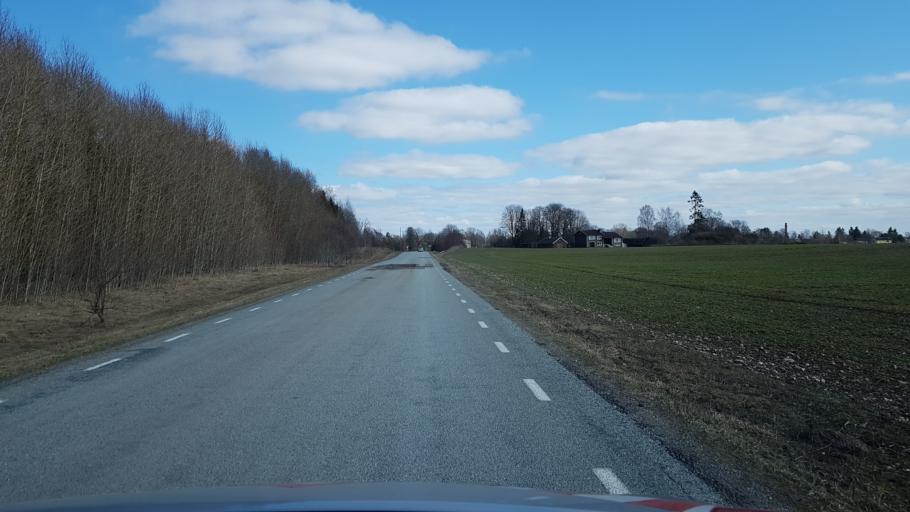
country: EE
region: Laeaene-Virumaa
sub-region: Tapa vald
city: Tapa
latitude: 59.2527
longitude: 25.8116
